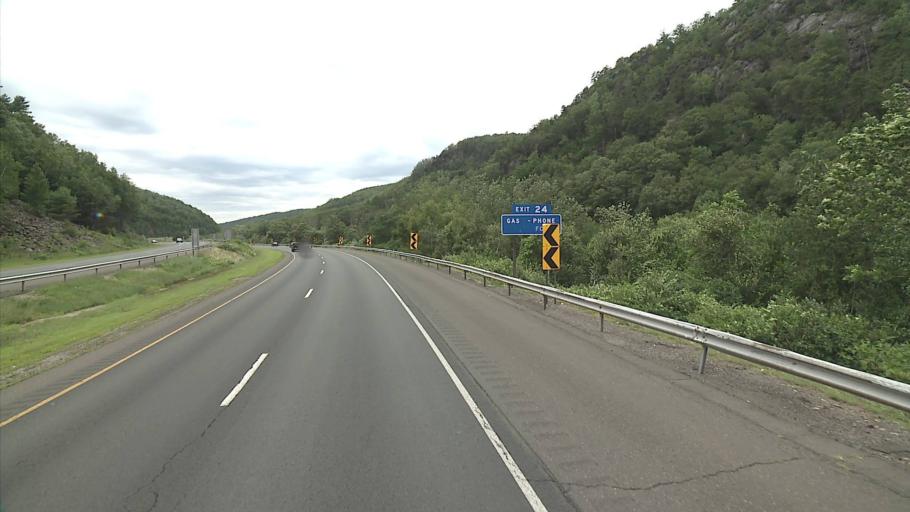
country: US
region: Connecticut
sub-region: New Haven County
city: Naugatuck
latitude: 41.4582
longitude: -73.0589
